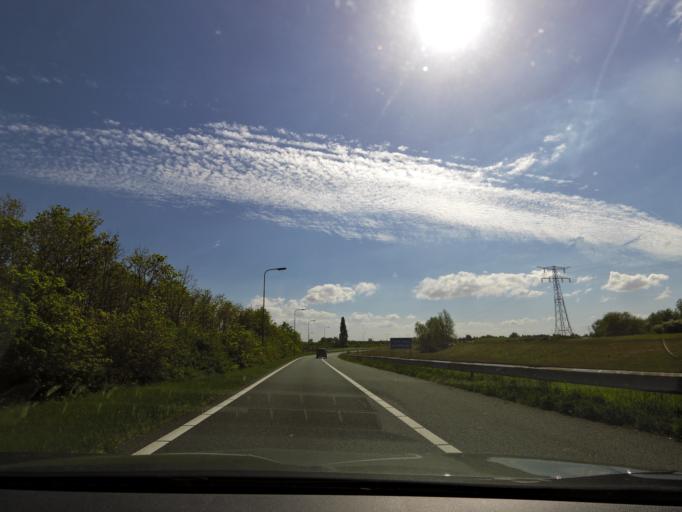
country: NL
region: North Brabant
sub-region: Gemeente Moerdijk
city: Willemstad
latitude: 51.7040
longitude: 4.3936
